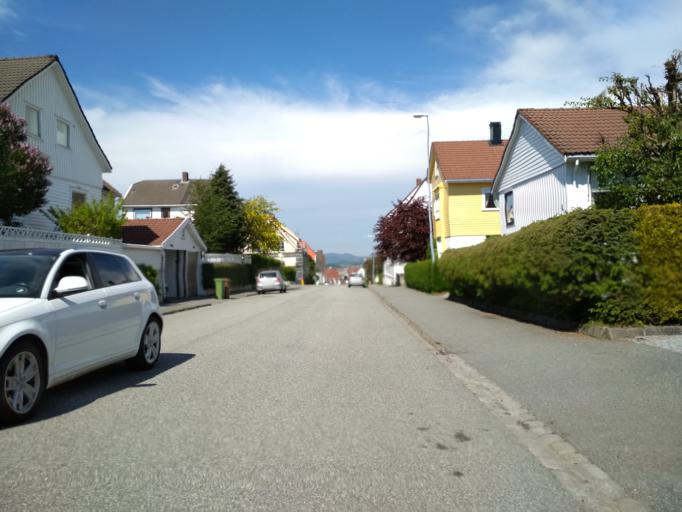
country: NO
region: Rogaland
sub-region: Stavanger
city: Stavanger
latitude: 58.9570
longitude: 5.7336
